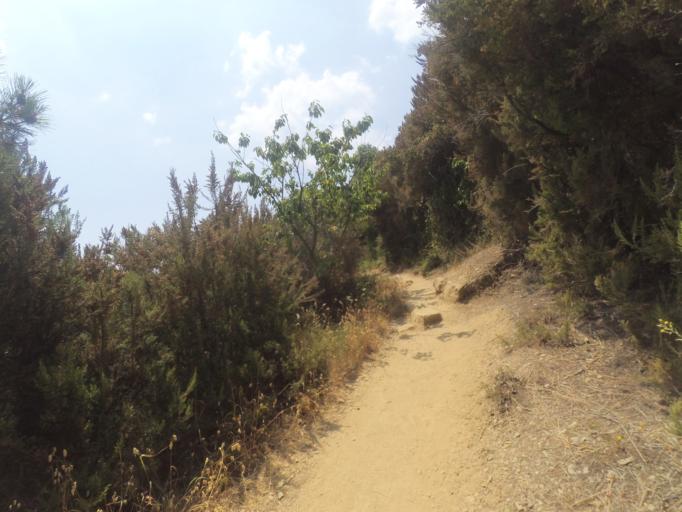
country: IT
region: Liguria
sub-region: Provincia di La Spezia
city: Riomaggiore
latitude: 44.1107
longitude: 9.7329
